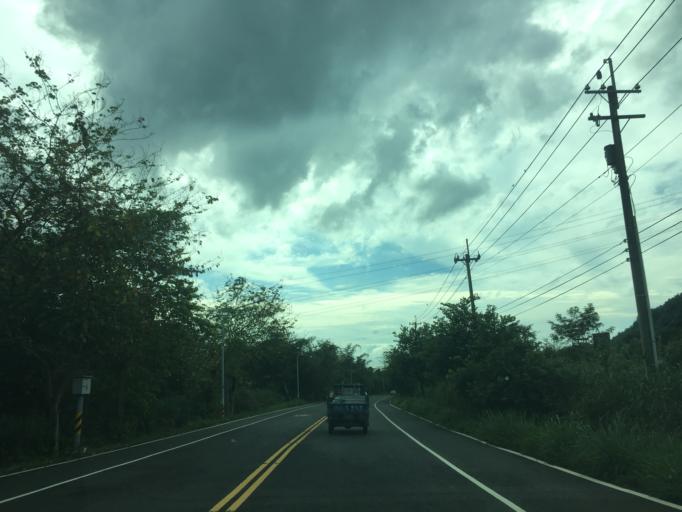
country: TW
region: Taiwan
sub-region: Chiayi
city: Jiayi Shi
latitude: 23.4415
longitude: 120.5977
